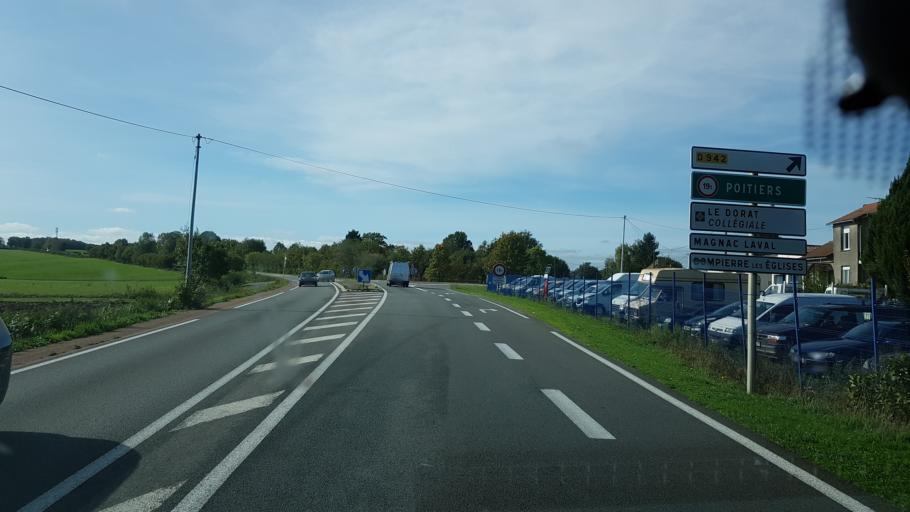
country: FR
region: Limousin
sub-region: Departement de la Haute-Vienne
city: Chateauponsac
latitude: 46.1925
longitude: 1.2392
